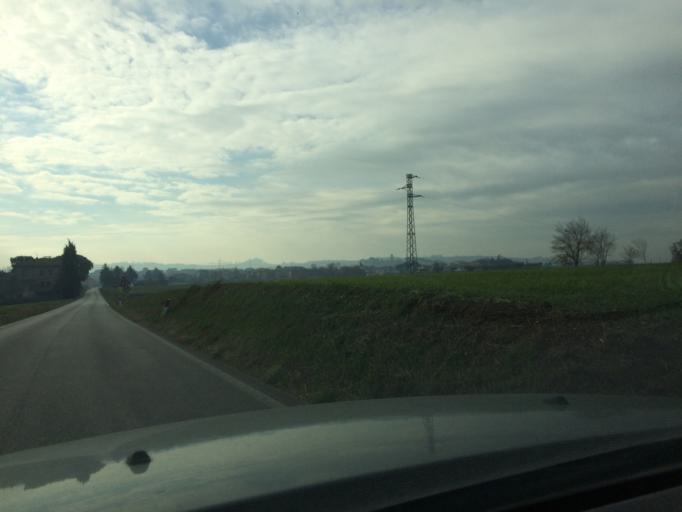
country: IT
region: Umbria
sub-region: Provincia di Perugia
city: Via Lippia
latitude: 43.0930
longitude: 12.4892
